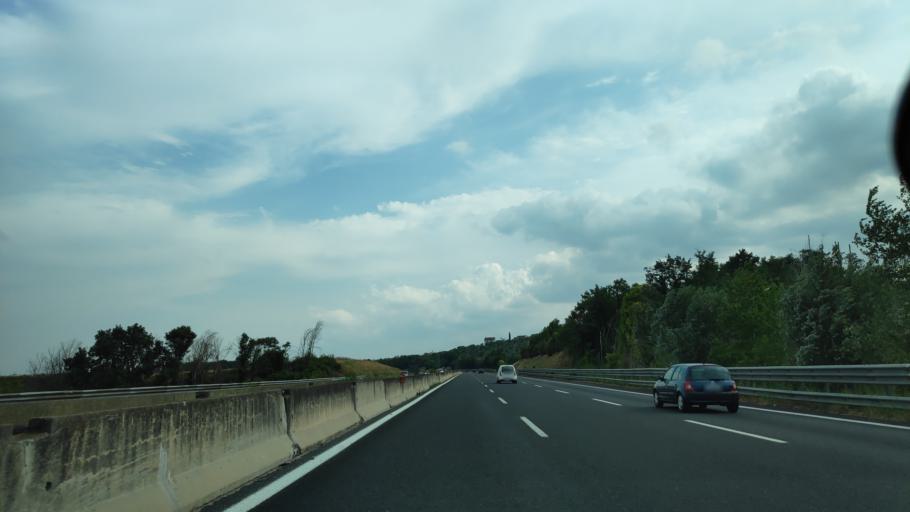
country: IT
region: Latium
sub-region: Citta metropolitana di Roma Capitale
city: Civitella San Paolo
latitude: 42.1857
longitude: 12.6027
